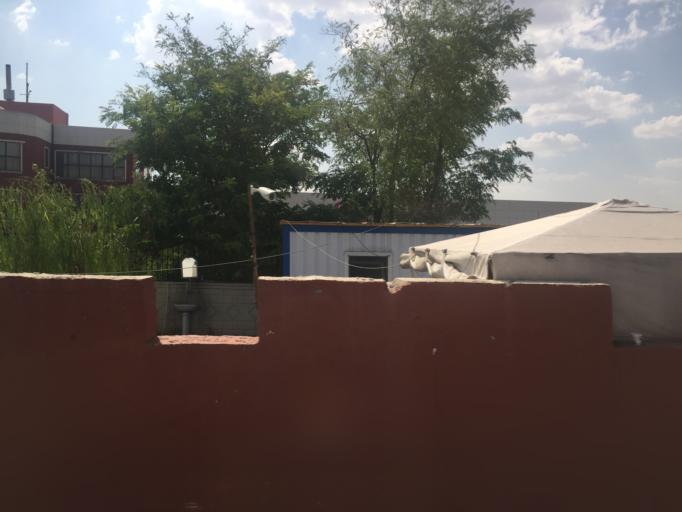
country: TR
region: Sanliurfa
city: Sanliurfa
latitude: 37.2392
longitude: 38.7940
